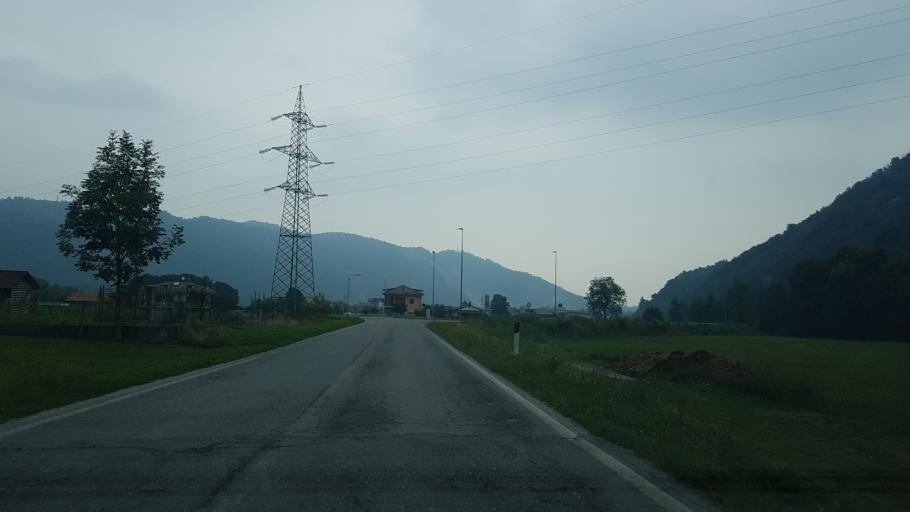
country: IT
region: Piedmont
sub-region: Provincia di Cuneo
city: Roccaforte Mondovi
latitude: 44.3076
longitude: 7.7457
